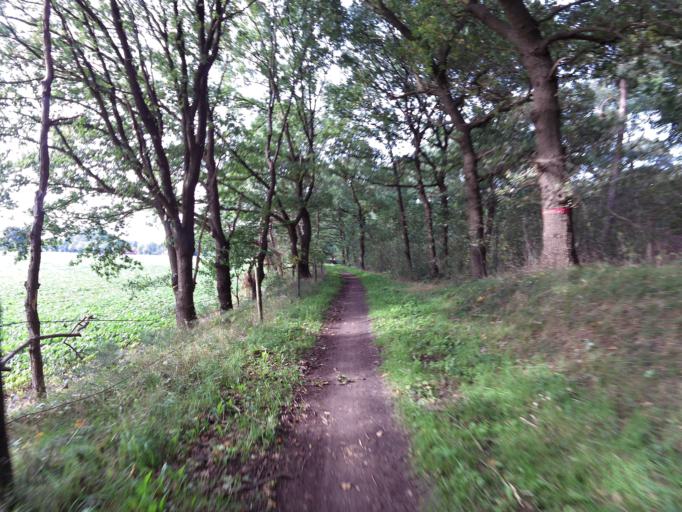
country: NL
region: Gelderland
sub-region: Gemeente Doetinchem
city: Doetinchem
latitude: 51.9832
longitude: 6.2642
